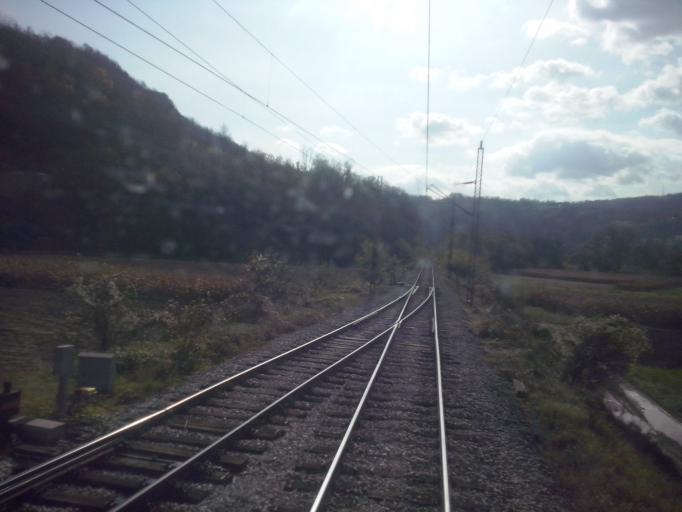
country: RS
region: Central Serbia
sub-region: Zlatiborski Okrug
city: Pozega
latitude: 43.9246
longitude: 19.9901
